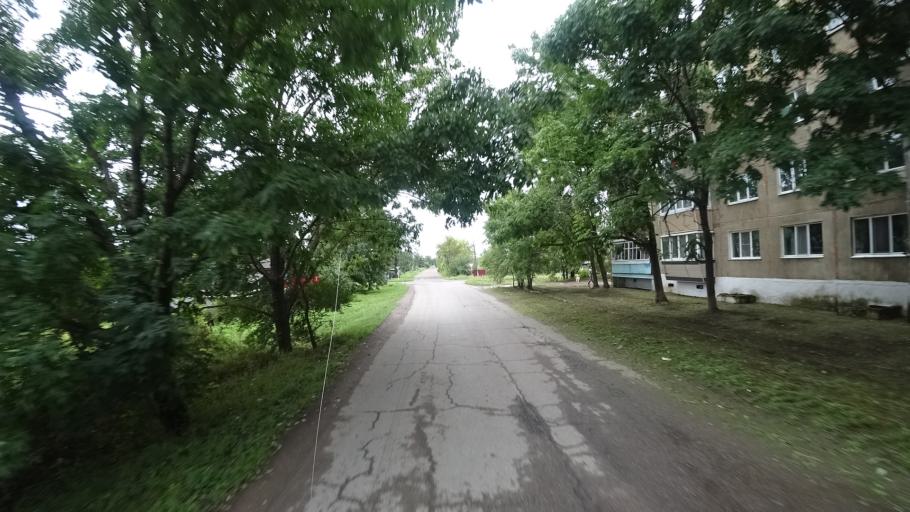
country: RU
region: Primorskiy
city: Chernigovka
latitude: 44.3419
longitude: 132.5697
